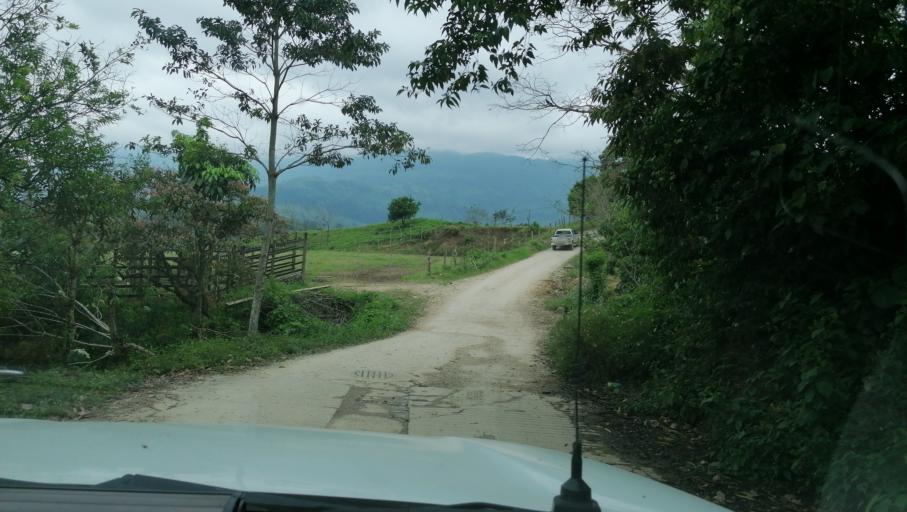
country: MX
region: Chiapas
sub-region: Ocotepec
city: San Pablo Huacano
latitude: 17.2725
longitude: -93.2431
